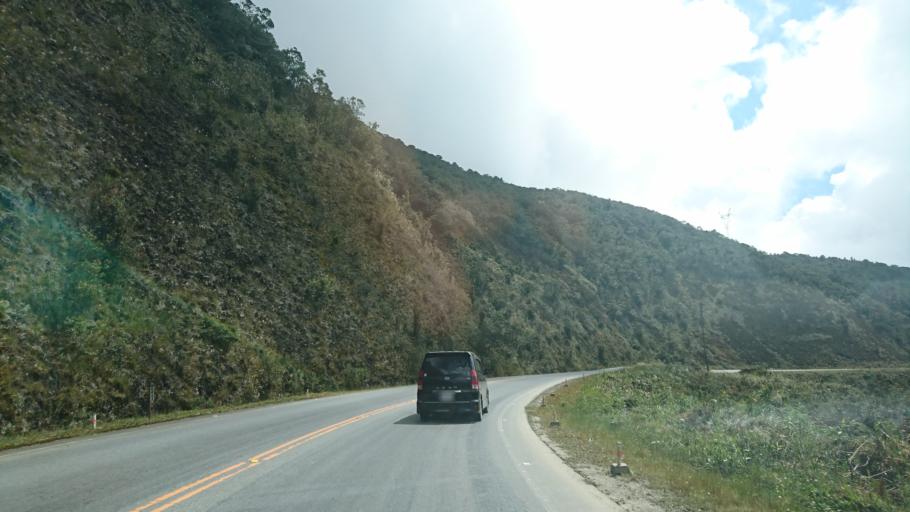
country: BO
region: La Paz
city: Coroico
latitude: -16.2906
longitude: -67.8550
